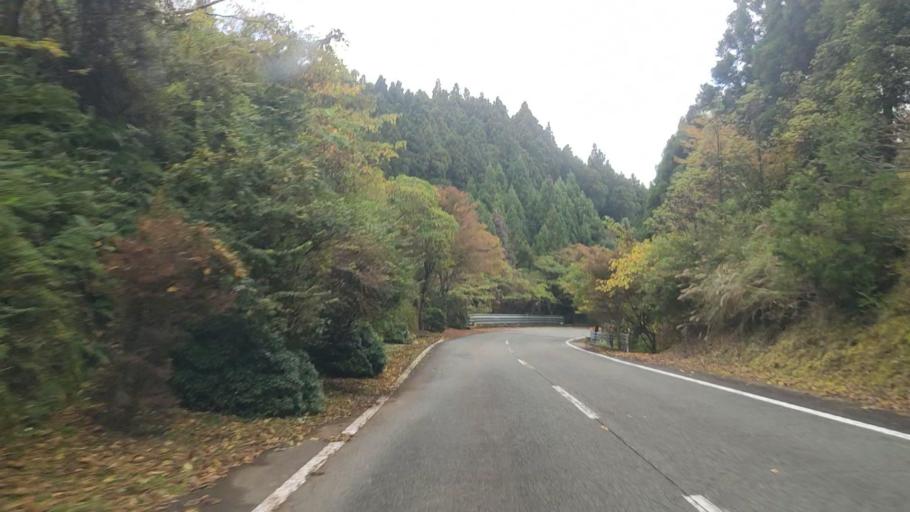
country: JP
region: Shizuoka
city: Heda
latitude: 34.9129
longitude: 138.8478
